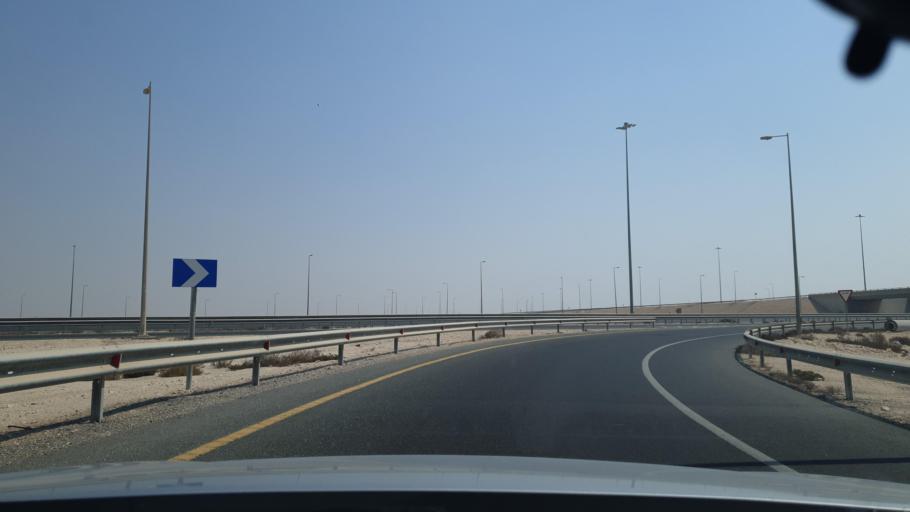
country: QA
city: Al Ghuwayriyah
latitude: 25.8310
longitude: 51.3491
